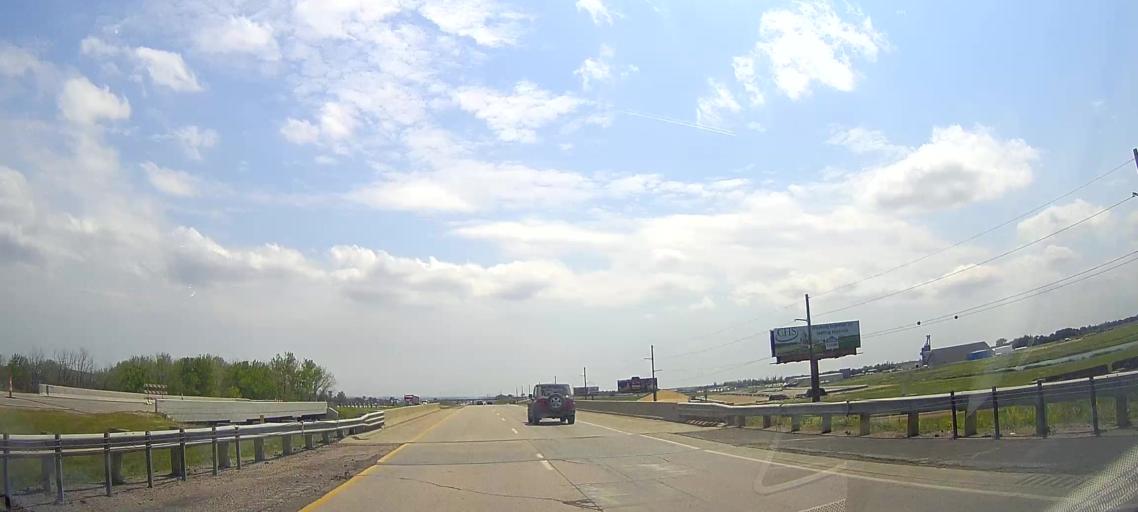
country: US
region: South Dakota
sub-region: Lincoln County
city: Lennox
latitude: 43.3382
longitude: -96.7966
